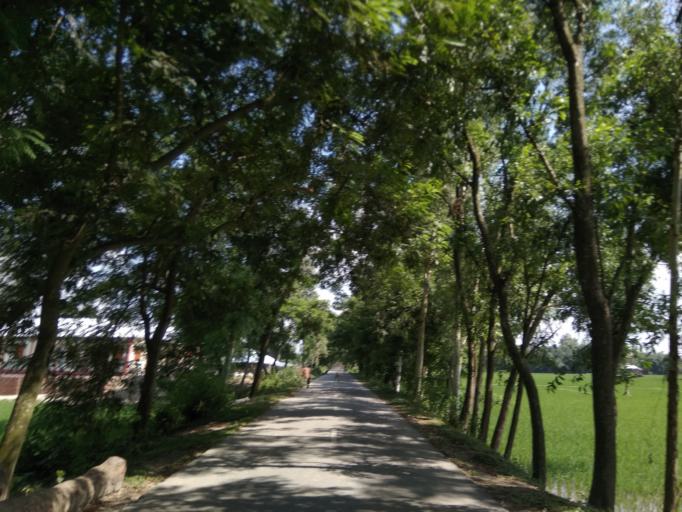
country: IN
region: West Bengal
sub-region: Koch Bihar
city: Haldibari
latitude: 26.1970
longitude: 88.6886
